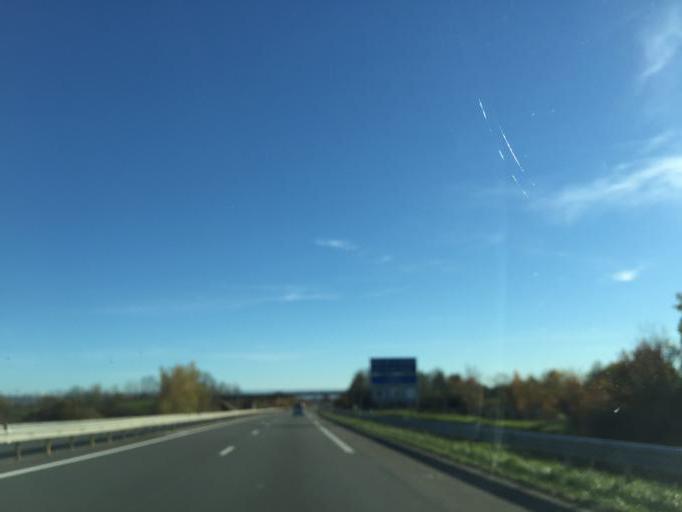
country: FR
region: Rhone-Alpes
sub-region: Departement de la Loire
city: Balbigny
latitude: 45.7662
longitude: 4.1596
